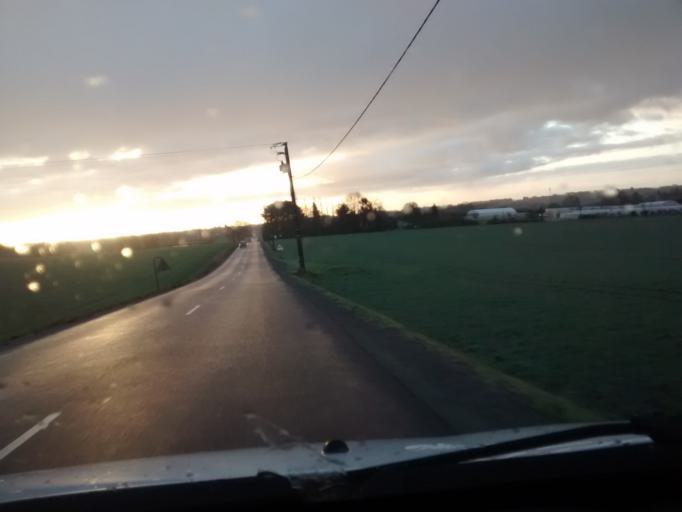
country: FR
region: Brittany
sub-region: Departement d'Ille-et-Vilaine
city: Bais
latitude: 48.0231
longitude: -1.3084
